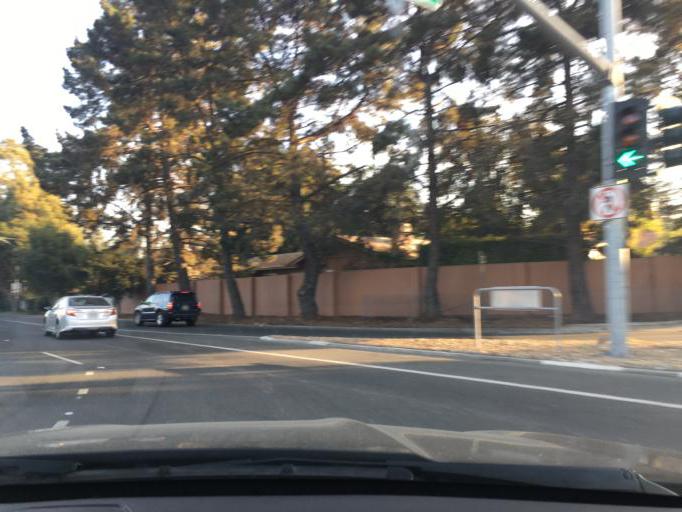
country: US
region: California
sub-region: Santa Clara County
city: Loyola
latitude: 37.3455
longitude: -122.0780
